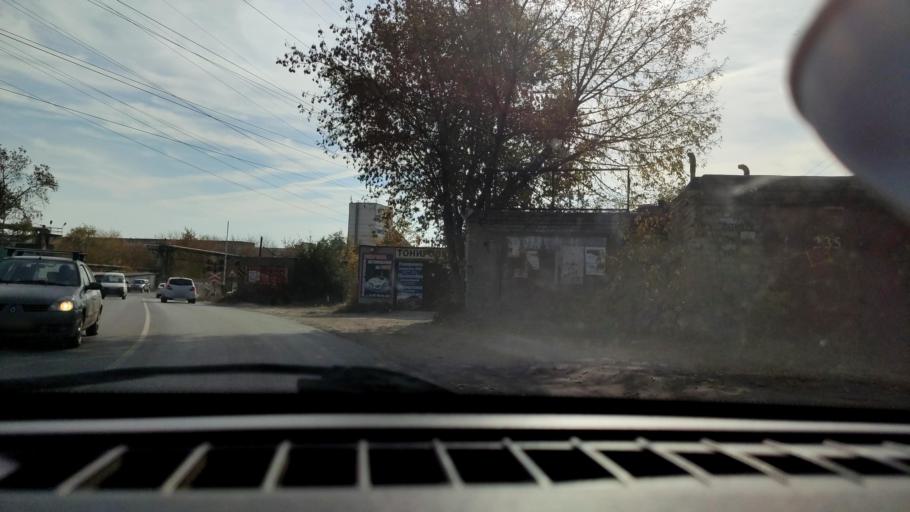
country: RU
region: Samara
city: Petra-Dubrava
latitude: 53.2520
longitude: 50.2945
